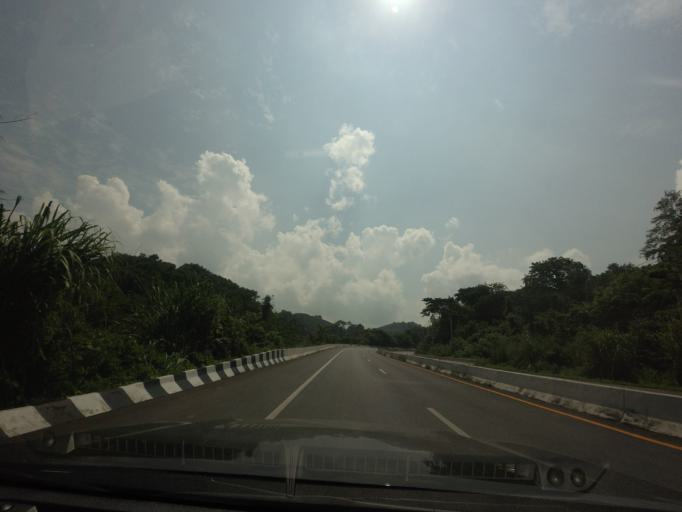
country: TH
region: Phrae
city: Den Chai
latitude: 17.8749
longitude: 100.0456
